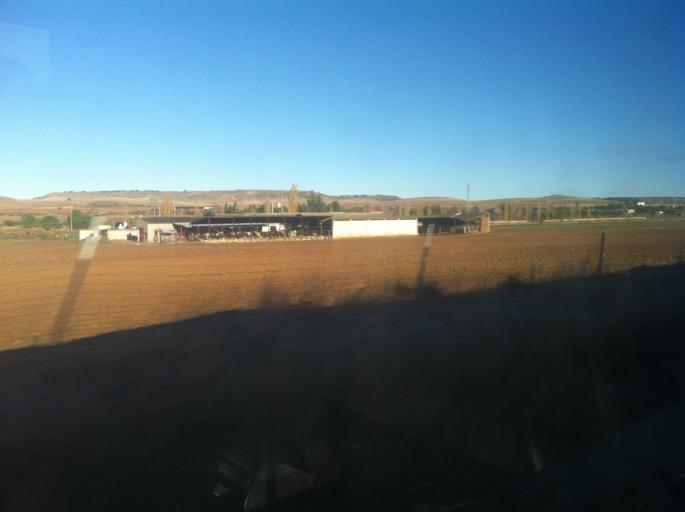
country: ES
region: Castille and Leon
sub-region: Provincia de Palencia
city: Duenas
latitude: 41.8445
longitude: -4.5575
